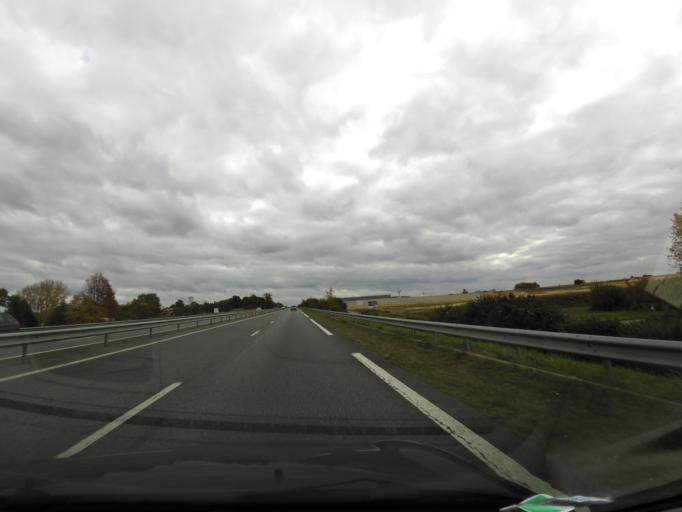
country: FR
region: Brittany
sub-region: Departement d'Ille-et-Vilaine
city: Saint-Armel
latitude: 48.0124
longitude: -1.6006
